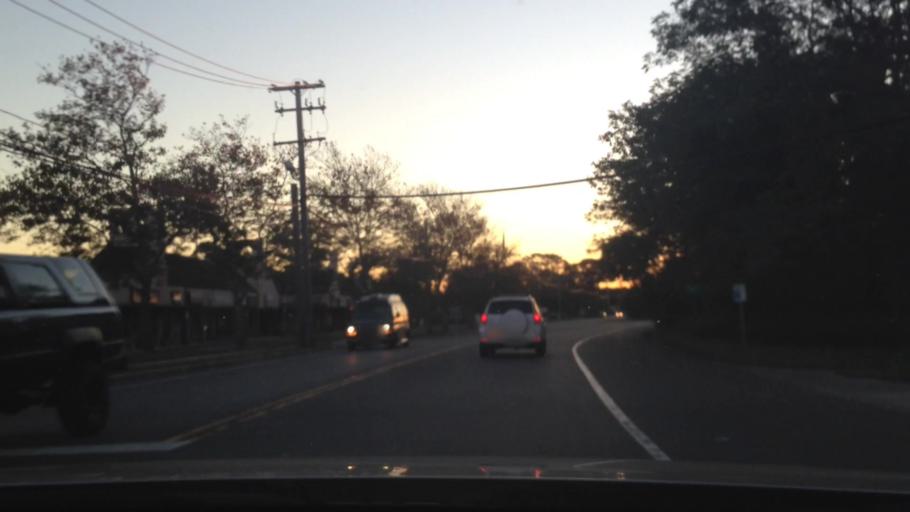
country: US
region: New York
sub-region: Suffolk County
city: Port Jefferson Station
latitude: 40.9331
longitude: -73.0356
